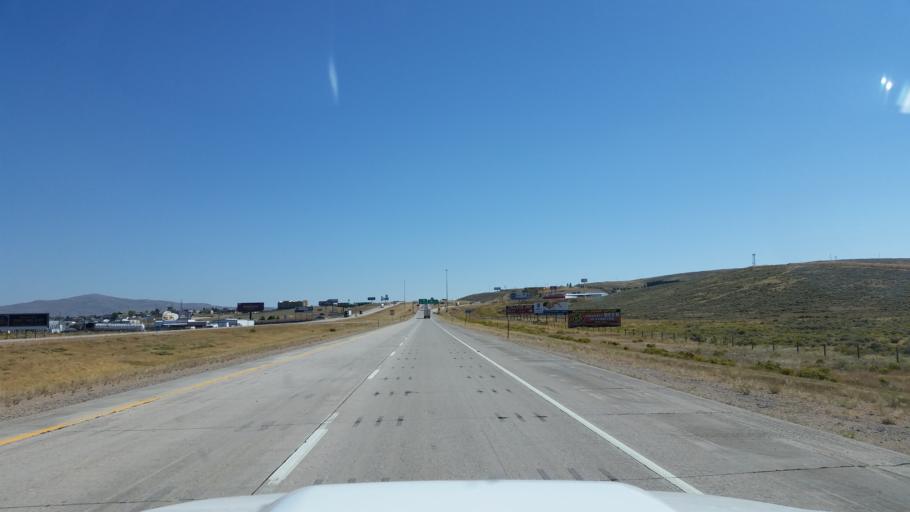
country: US
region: Wyoming
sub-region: Uinta County
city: Evanston
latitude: 41.2546
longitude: -110.9987
